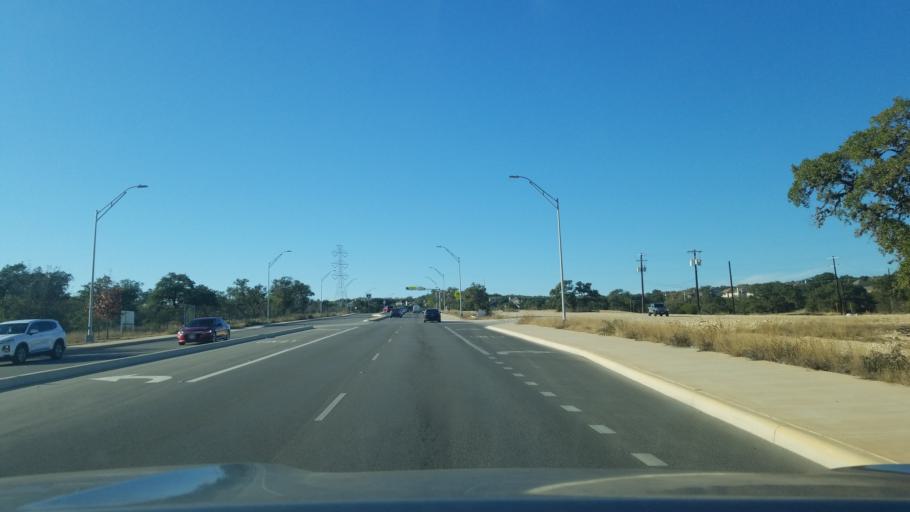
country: US
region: Texas
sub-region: Bexar County
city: Hollywood Park
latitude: 29.6290
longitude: -98.4784
